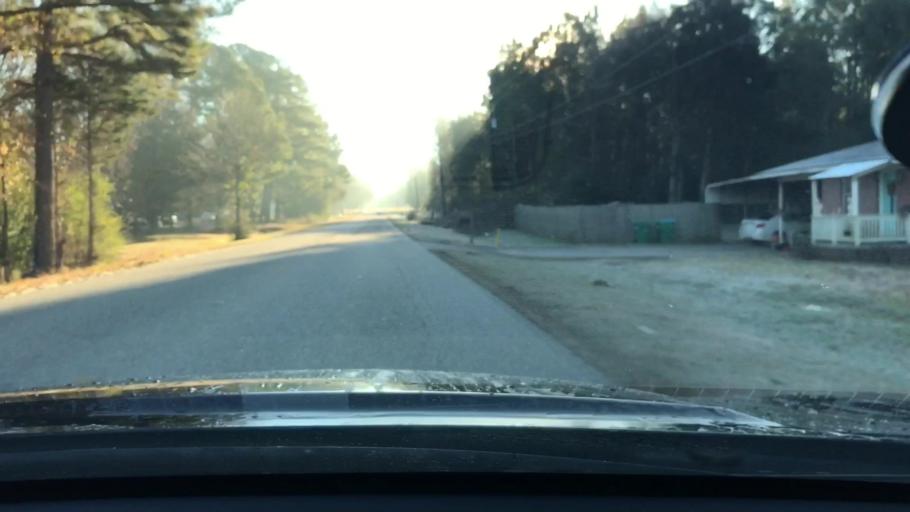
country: US
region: Alabama
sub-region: Talladega County
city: Mignon
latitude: 33.2116
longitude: -86.2971
